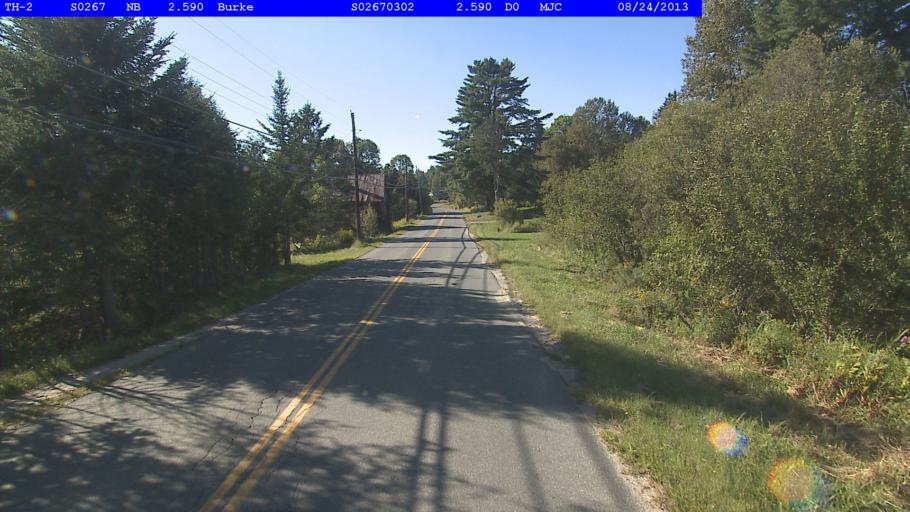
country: US
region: Vermont
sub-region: Caledonia County
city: Lyndonville
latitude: 44.6207
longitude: -71.9470
